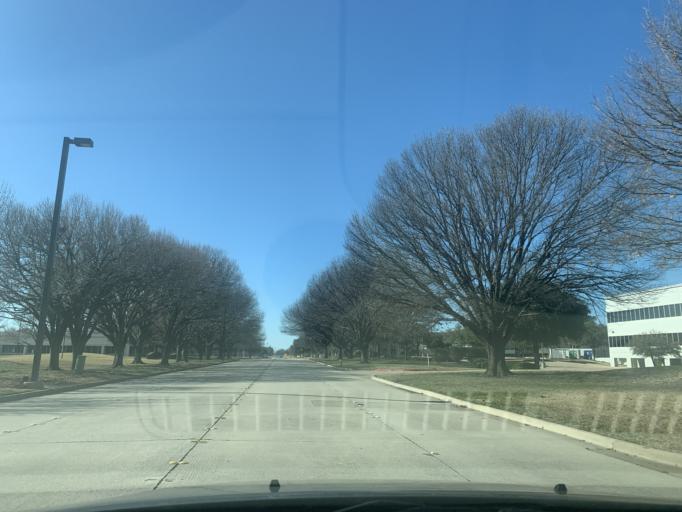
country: US
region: Texas
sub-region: Denton County
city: The Colony
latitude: 33.0686
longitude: -96.8134
